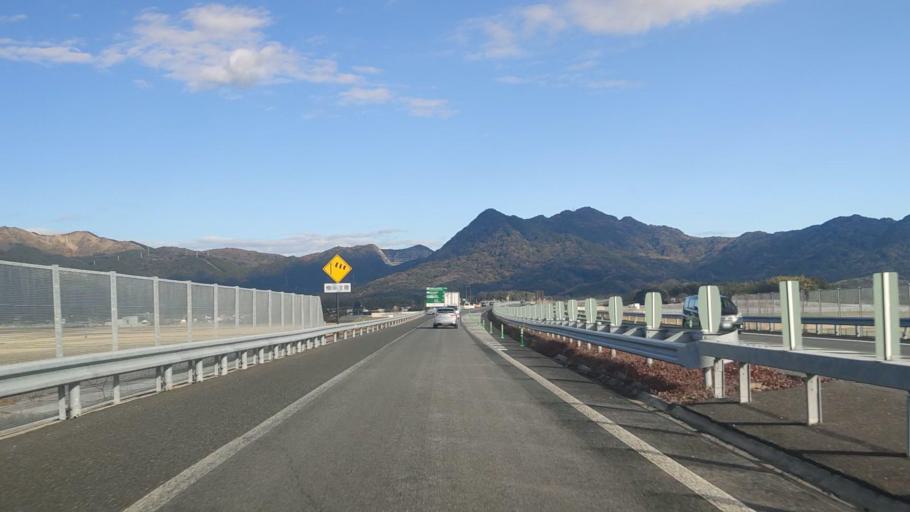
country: JP
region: Fukuoka
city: Yukuhashi
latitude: 33.7328
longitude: 130.9472
